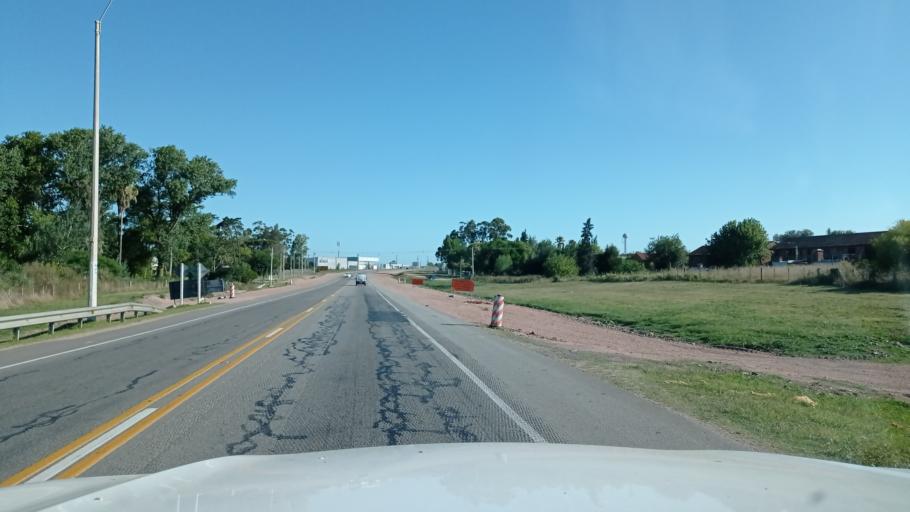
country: UY
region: Canelones
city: Pando
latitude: -34.7189
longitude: -55.9495
